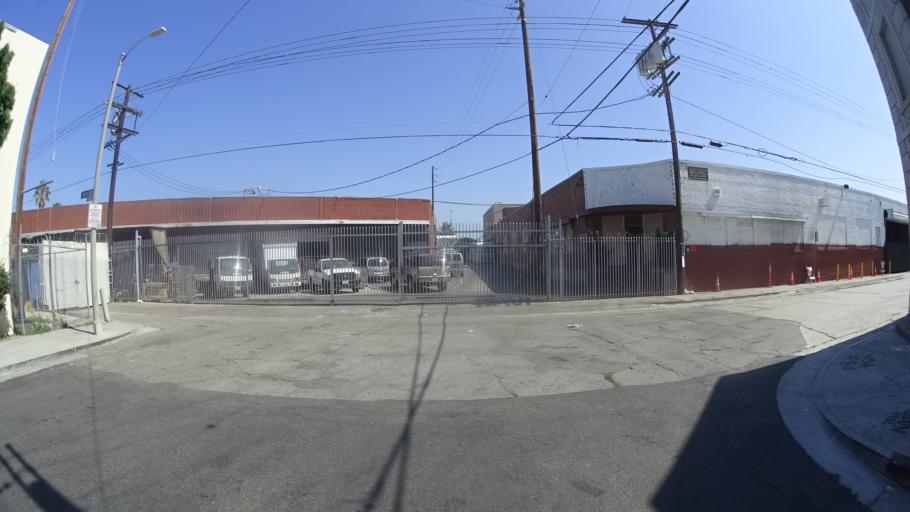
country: US
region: California
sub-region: Los Angeles County
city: View Park-Windsor Hills
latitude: 33.9851
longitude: -118.3134
